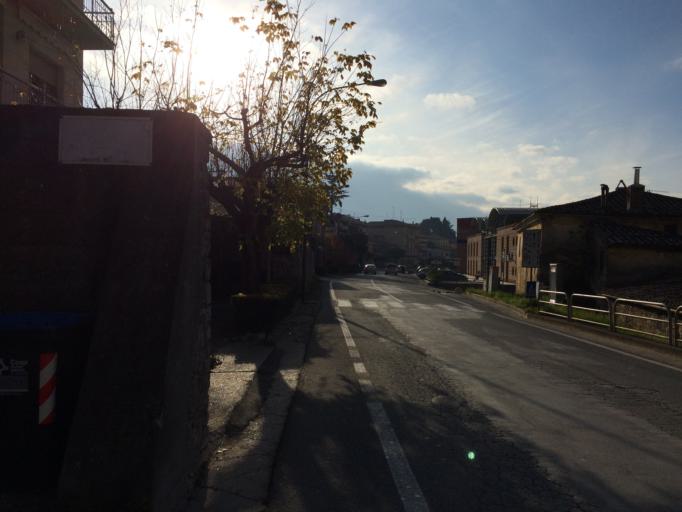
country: IT
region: Umbria
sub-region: Provincia di Terni
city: Amelia
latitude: 42.5511
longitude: 12.4181
